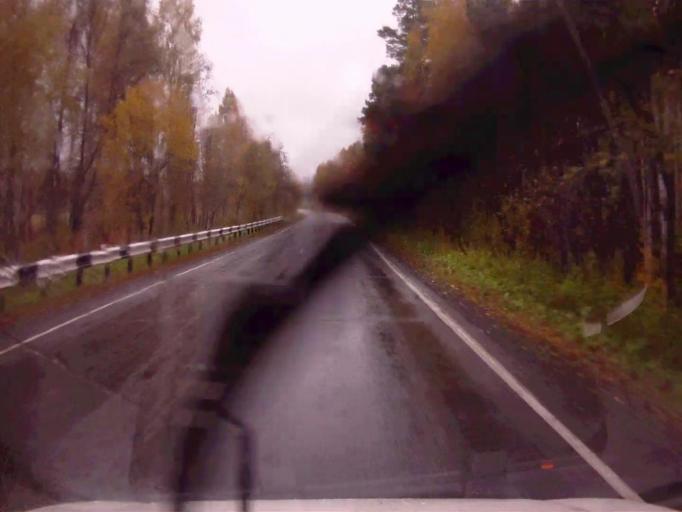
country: RU
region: Chelyabinsk
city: Verkhniy Ufaley
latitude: 55.9422
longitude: 60.4088
